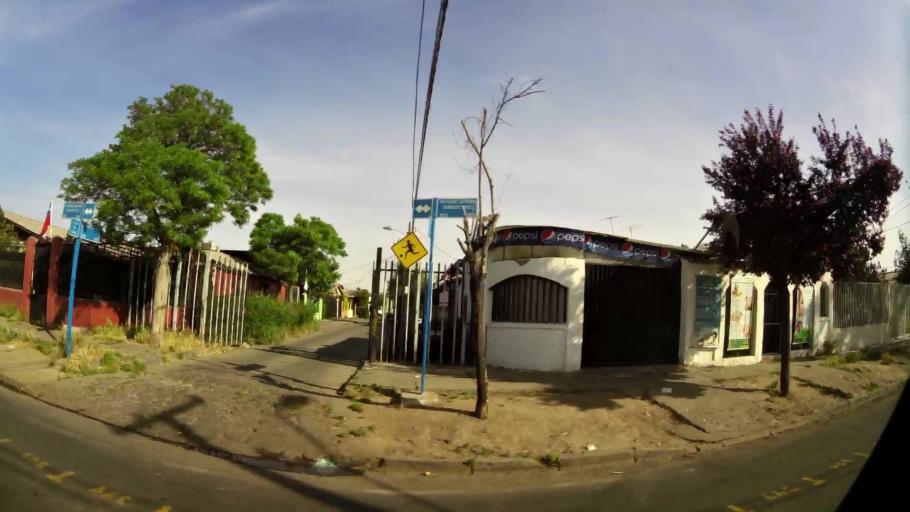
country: CL
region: Santiago Metropolitan
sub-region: Provincia de Santiago
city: La Pintana
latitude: -33.5207
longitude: -70.6308
